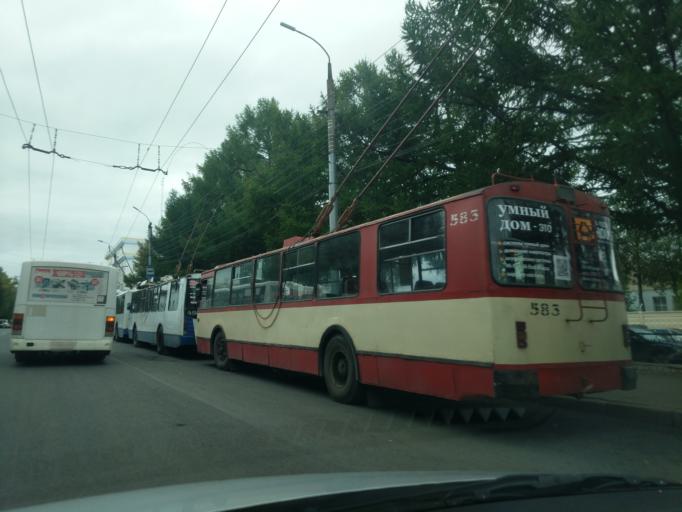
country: RU
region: Kirov
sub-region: Kirovo-Chepetskiy Rayon
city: Kirov
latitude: 58.6376
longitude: 49.6119
